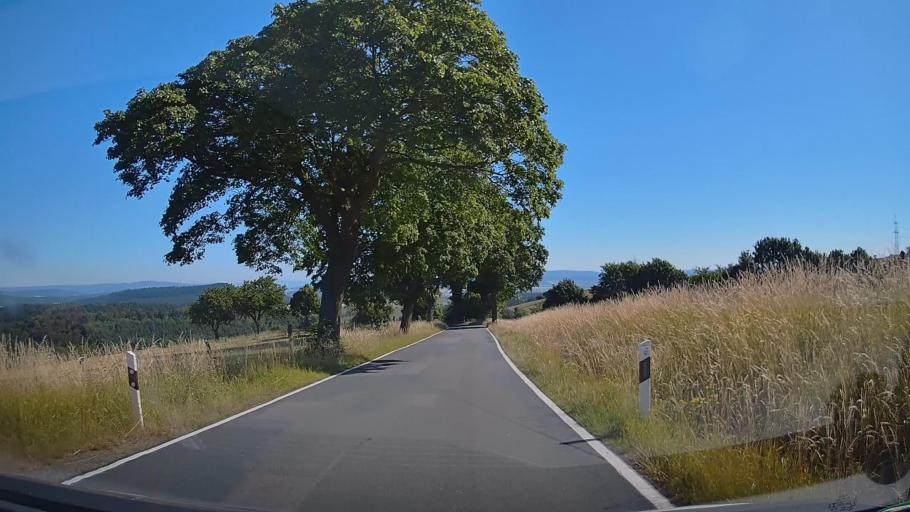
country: DE
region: Lower Saxony
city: Vahlbruch
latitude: 51.9721
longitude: 9.3542
